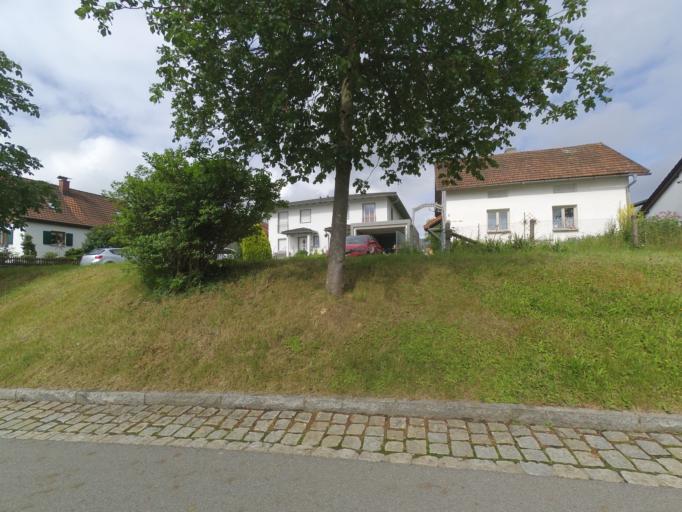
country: DE
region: Bavaria
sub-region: Lower Bavaria
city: Mitterfels
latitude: 48.9750
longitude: 12.6803
